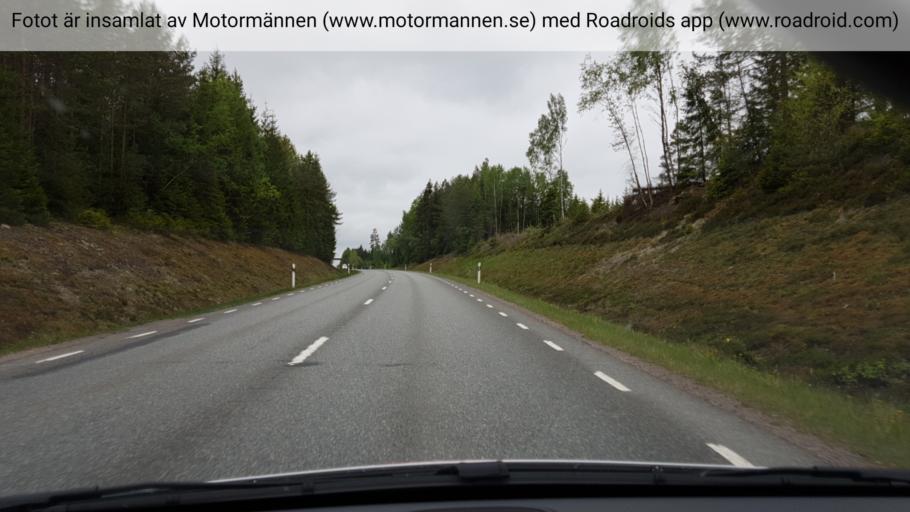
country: SE
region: Joenkoeping
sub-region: Jonkopings Kommun
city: Taberg
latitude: 57.6751
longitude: 13.8423
